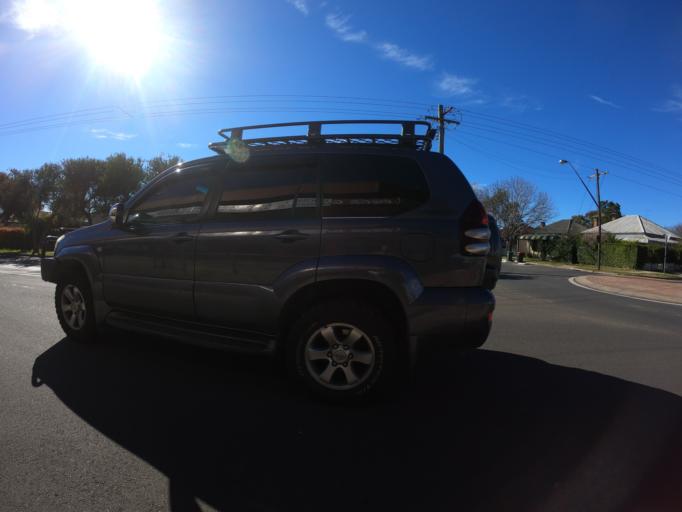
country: AU
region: New South Wales
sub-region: Hawkesbury
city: South Windsor
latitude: -33.6167
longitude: 150.8082
